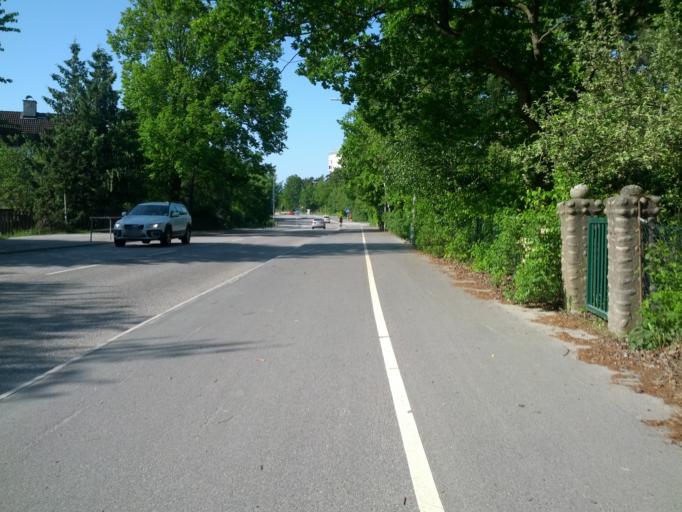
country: SE
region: Stockholm
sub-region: Danderyds Kommun
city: Djursholm
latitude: 59.3976
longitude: 18.0535
